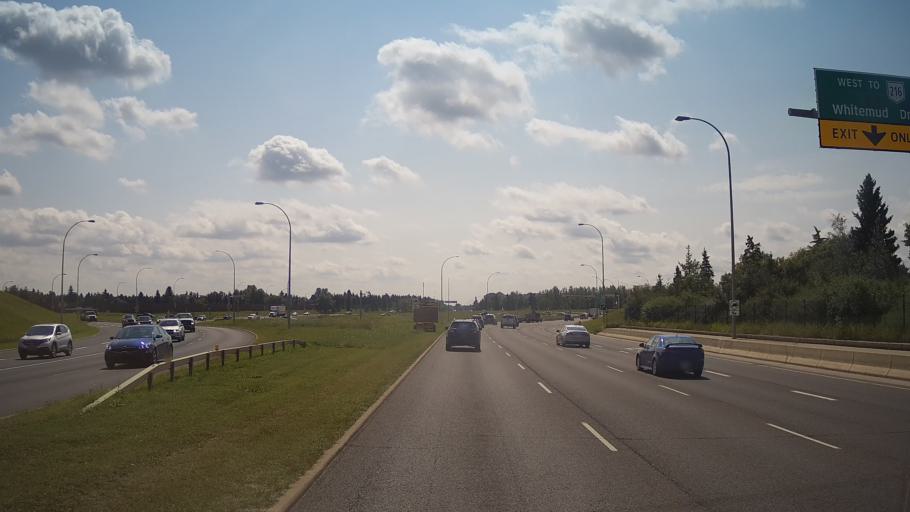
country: CA
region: Alberta
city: St. Albert
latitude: 53.5147
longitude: -113.6154
